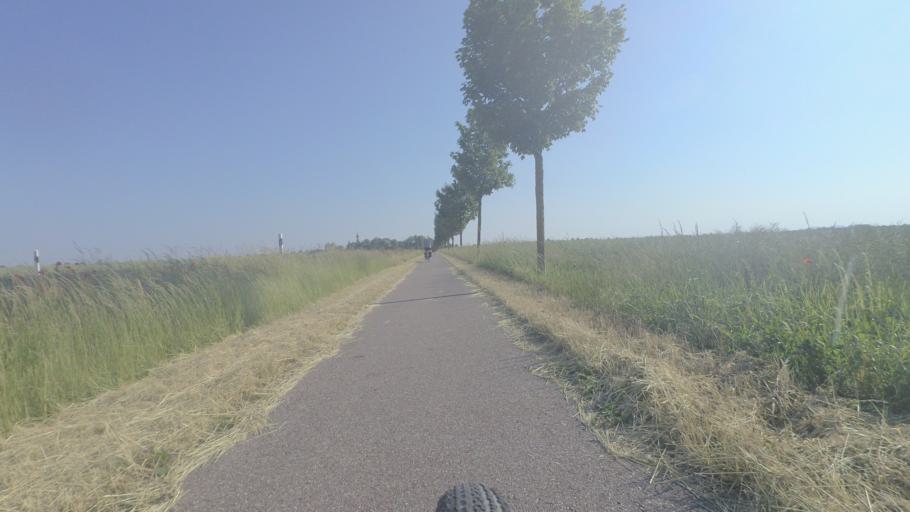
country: DE
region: Saxony-Anhalt
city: Osternienburger Land
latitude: 51.7865
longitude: 12.0085
